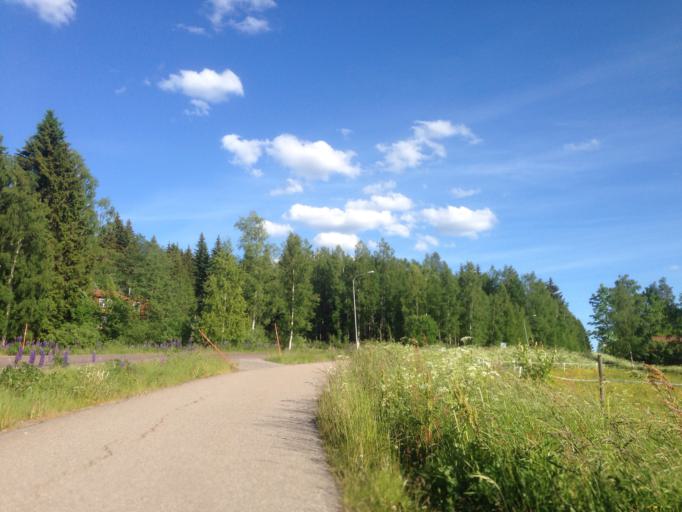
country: SE
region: Dalarna
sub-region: Ludvika Kommun
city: Ludvika
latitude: 60.1200
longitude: 15.2024
